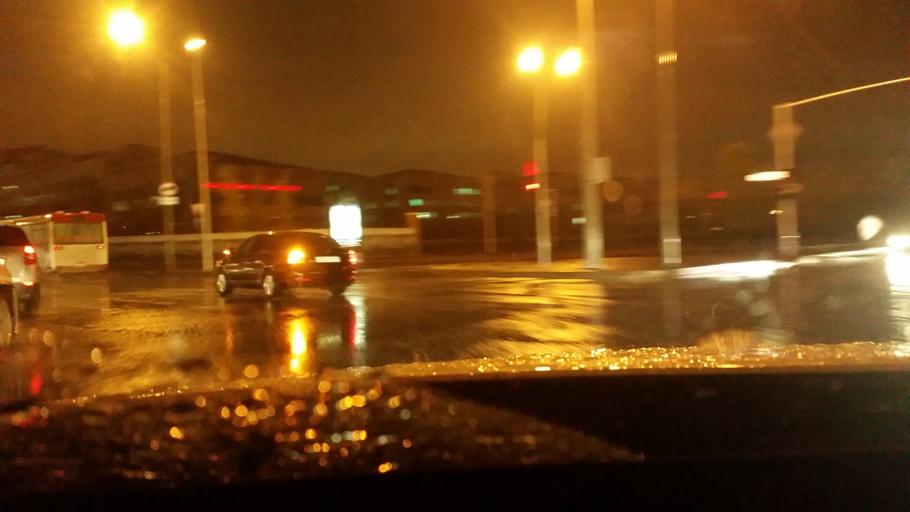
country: KZ
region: Astana Qalasy
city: Astana
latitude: 51.1270
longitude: 71.4047
